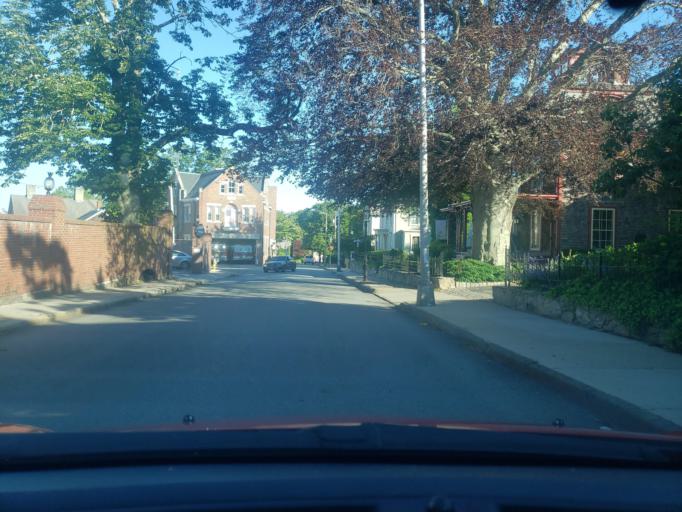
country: US
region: Rhode Island
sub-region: Newport County
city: Newport
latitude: 41.4880
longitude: -71.3100
